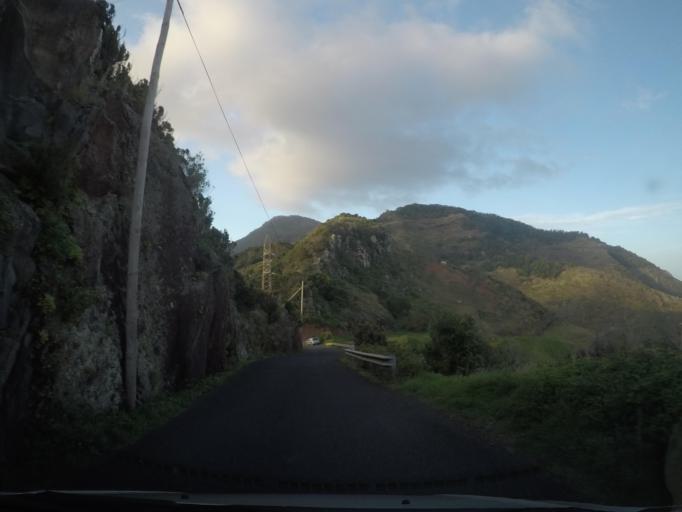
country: PT
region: Madeira
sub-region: Machico
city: Canical
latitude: 32.7250
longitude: -16.7592
